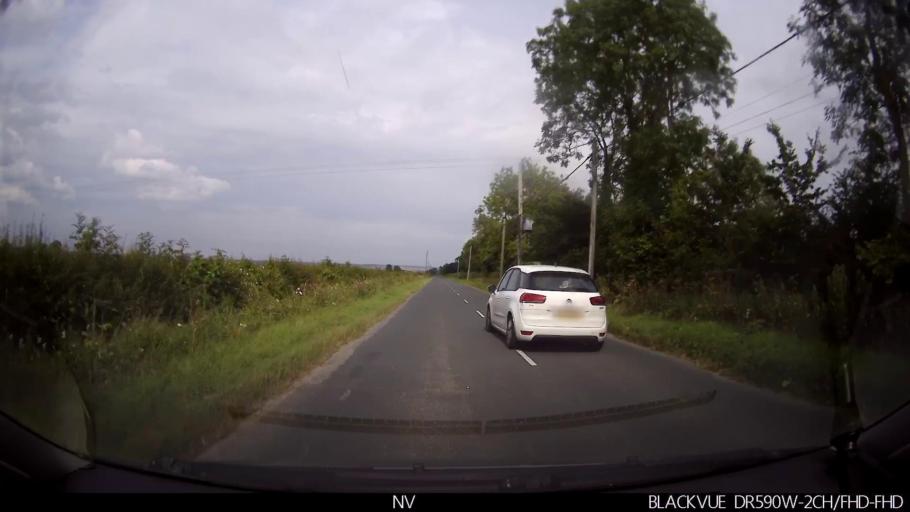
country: GB
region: England
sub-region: North Yorkshire
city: Marishes
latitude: 54.2080
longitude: -0.7883
